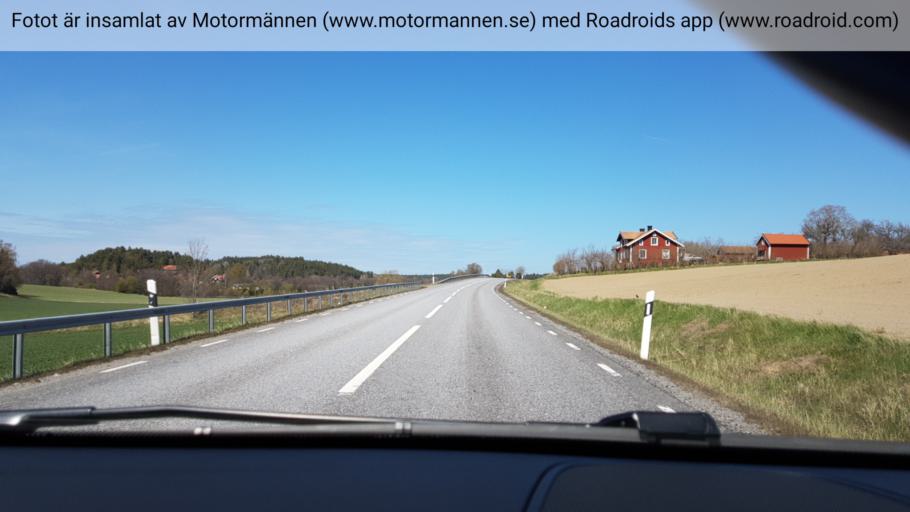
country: SE
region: Stockholm
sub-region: Nynashamns Kommun
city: Osmo
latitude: 59.0396
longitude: 17.8043
